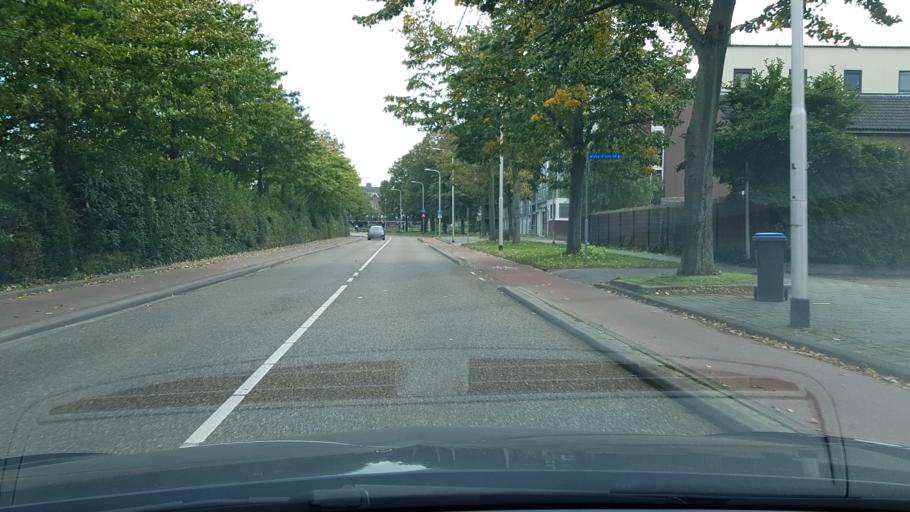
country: NL
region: South Holland
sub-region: Gemeente Hillegom
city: Hillegom
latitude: 52.2860
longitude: 4.5828
